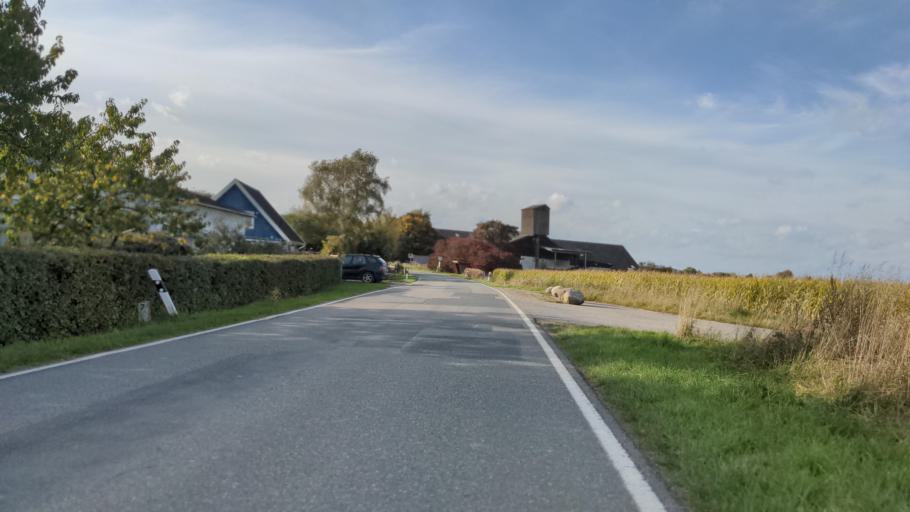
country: DE
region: Schleswig-Holstein
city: Monkhagen
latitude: 53.9542
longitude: 10.5387
